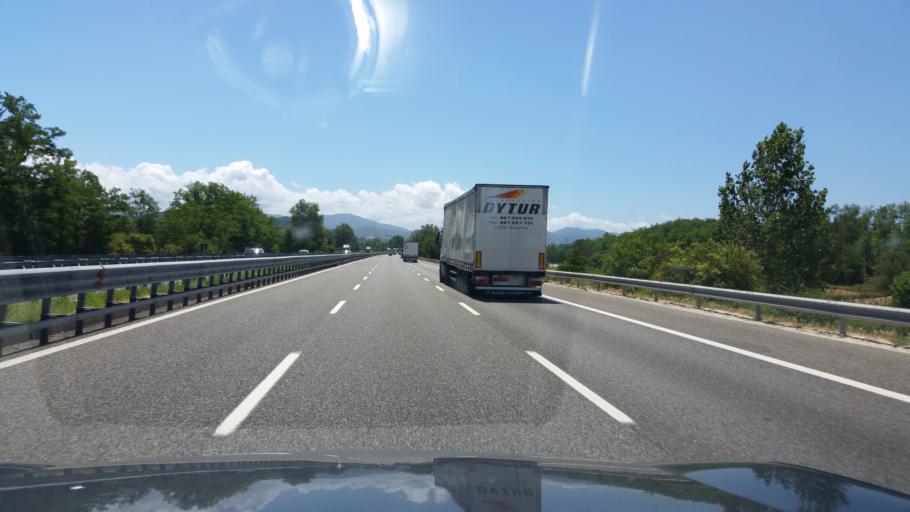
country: IT
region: Piedmont
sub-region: Provincia di Alessandria
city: Silvano d'Orba
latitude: 44.7117
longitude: 8.6668
